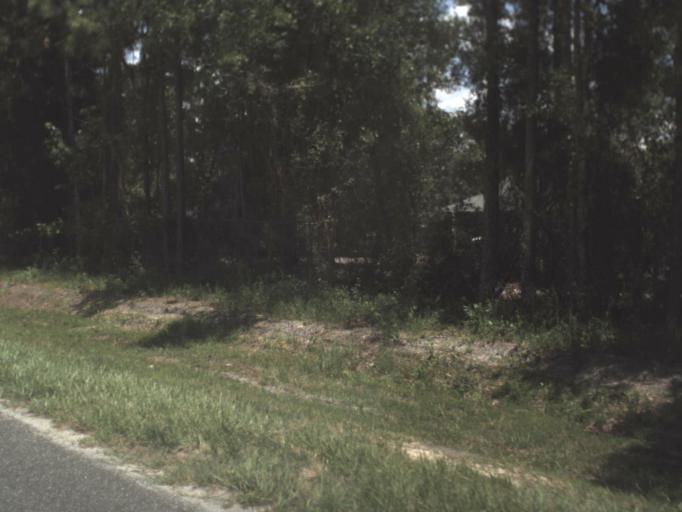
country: US
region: Florida
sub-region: Columbia County
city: Lake City
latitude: 30.1329
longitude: -82.7134
